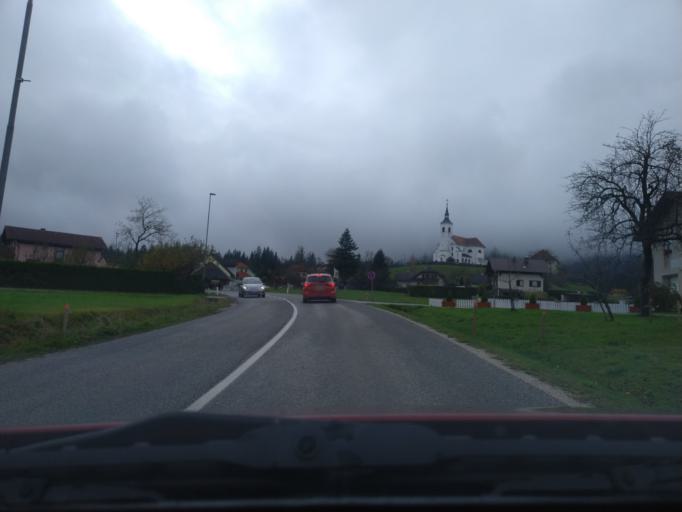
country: SI
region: Ljubno
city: Ljubno ob Savinji
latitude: 46.3270
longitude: 14.8483
